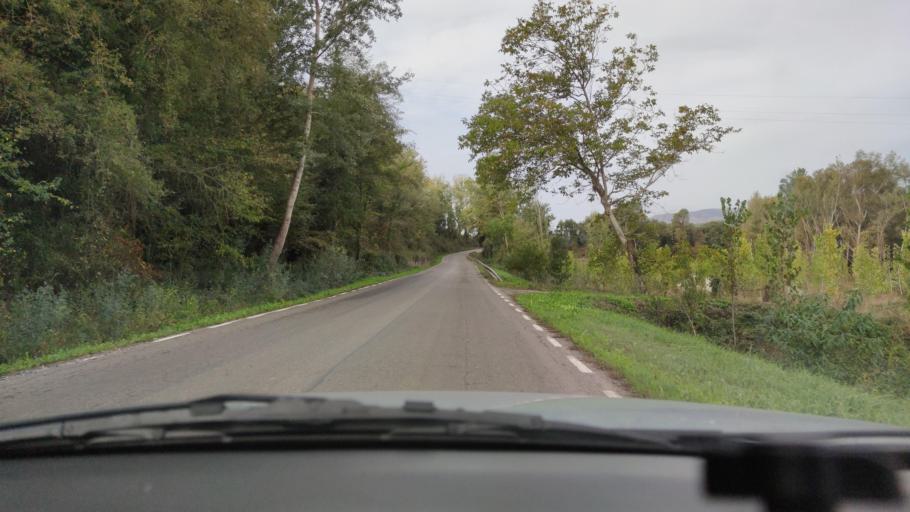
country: ES
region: Catalonia
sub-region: Provincia de Lleida
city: Artesa de Segre
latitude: 41.9189
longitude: 1.0916
